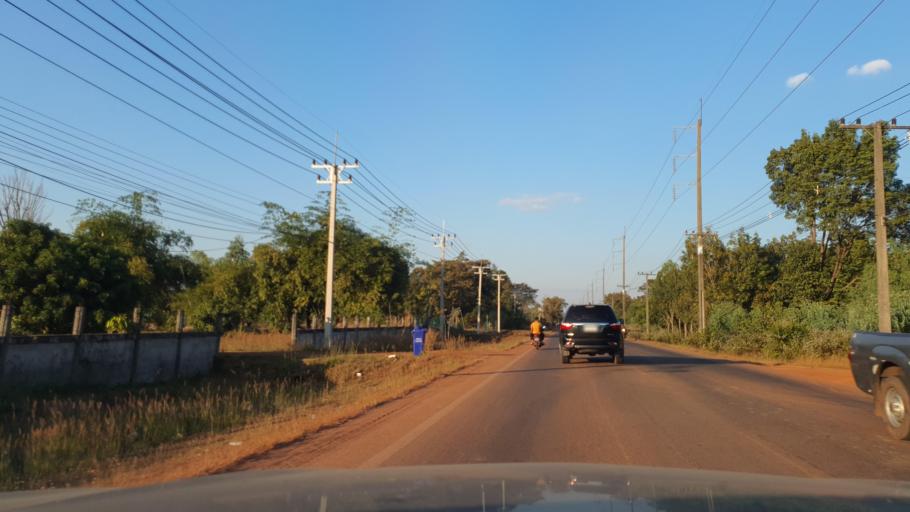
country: TH
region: Nakhon Phanom
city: Si Songkhram
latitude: 17.5964
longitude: 104.2374
